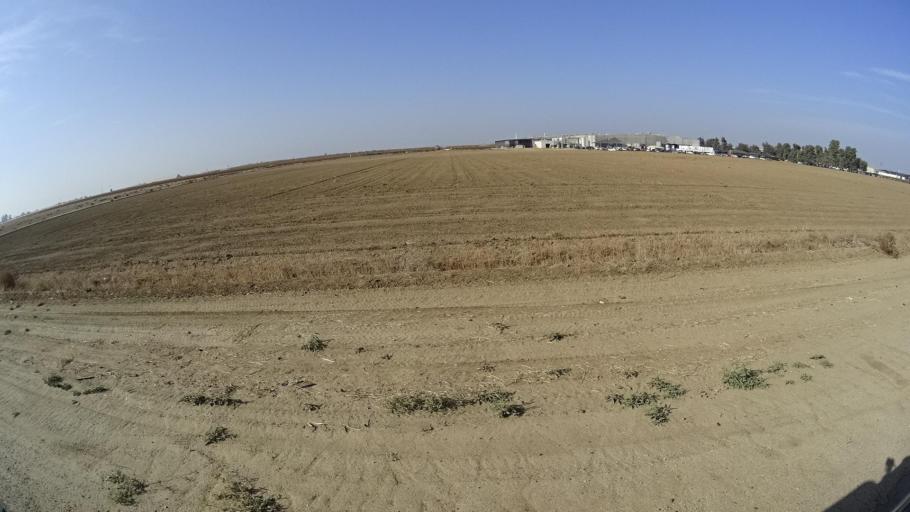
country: US
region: California
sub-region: Kern County
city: McFarland
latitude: 35.7008
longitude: -119.2230
